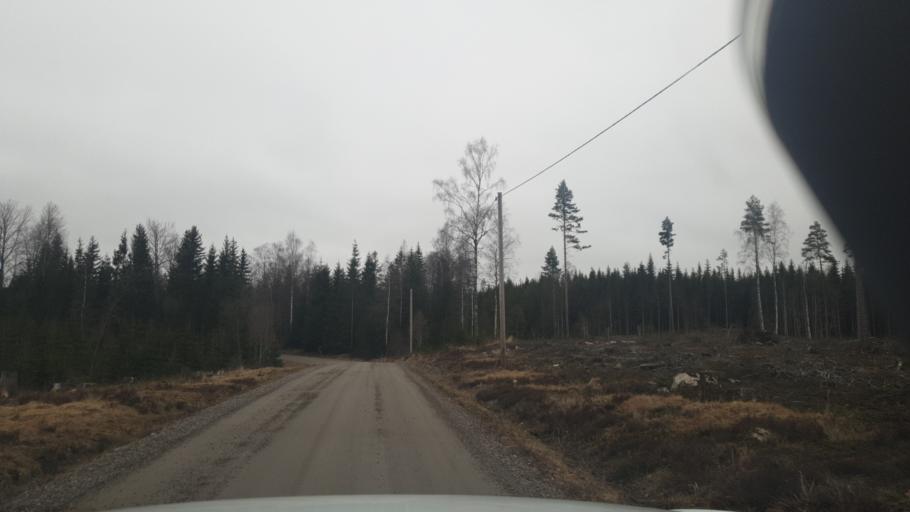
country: NO
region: Ostfold
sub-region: Romskog
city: Romskog
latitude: 59.7037
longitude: 12.0536
